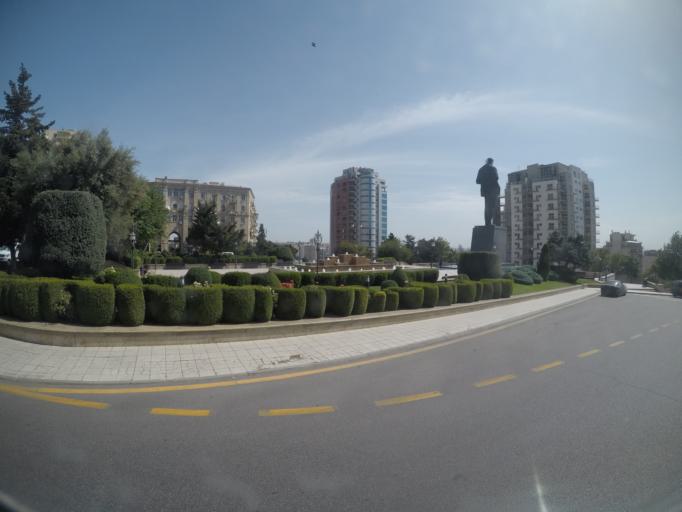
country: AZ
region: Baki
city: Badamdar
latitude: 40.3682
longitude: 49.8239
